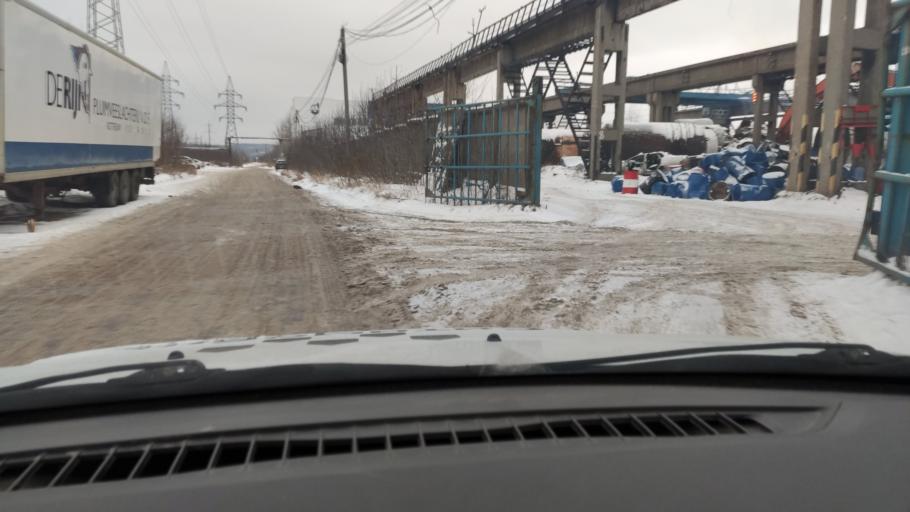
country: RU
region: Perm
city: Gamovo
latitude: 57.9218
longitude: 56.1533
